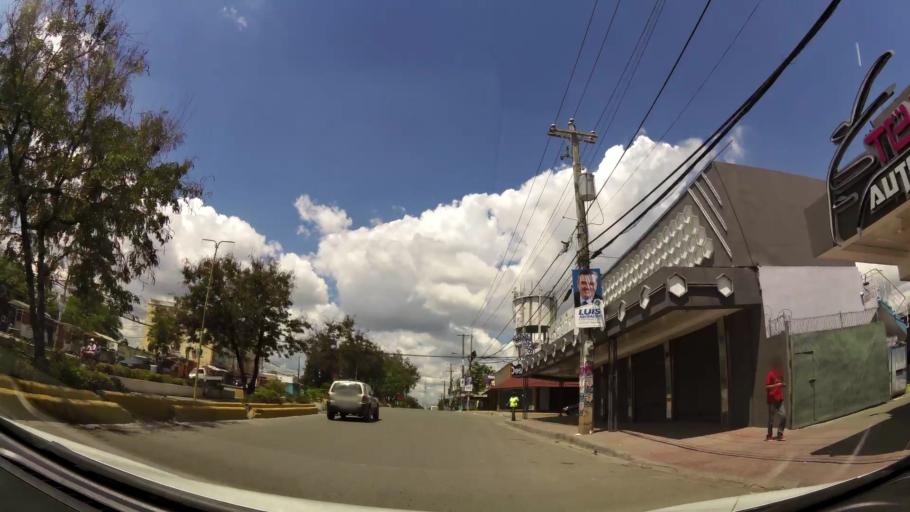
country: DO
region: Santo Domingo
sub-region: Santo Domingo
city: Santo Domingo Este
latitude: 18.5298
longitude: -69.8647
